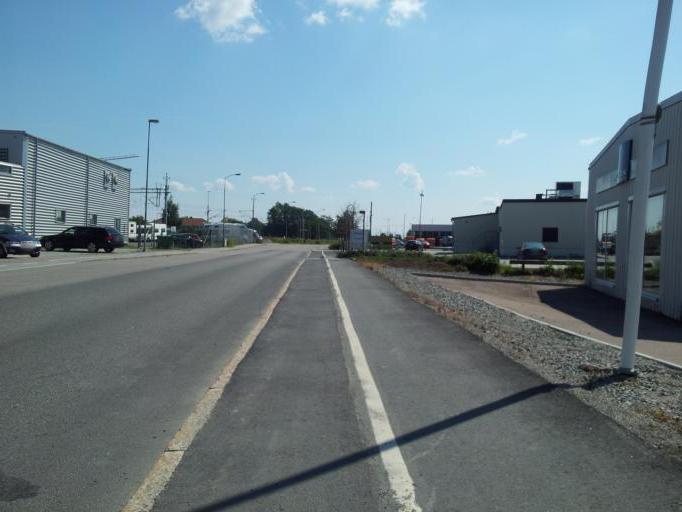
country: SE
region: Uppsala
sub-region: Uppsala Kommun
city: Uppsala
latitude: 59.8491
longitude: 17.6629
